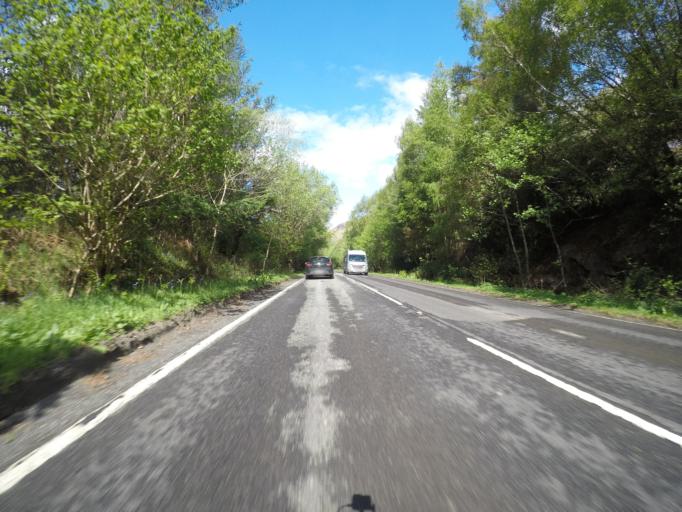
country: GB
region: Scotland
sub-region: Highland
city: Fort William
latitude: 57.2489
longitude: -5.4702
